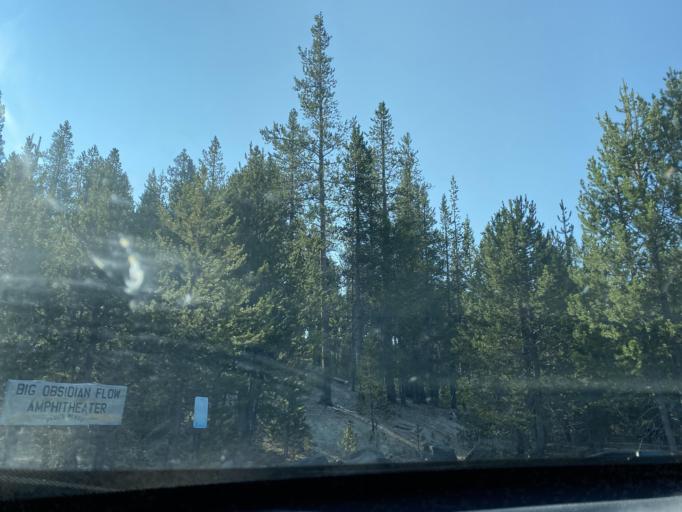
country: US
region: Oregon
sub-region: Deschutes County
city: Three Rivers
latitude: 43.7065
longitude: -121.2358
